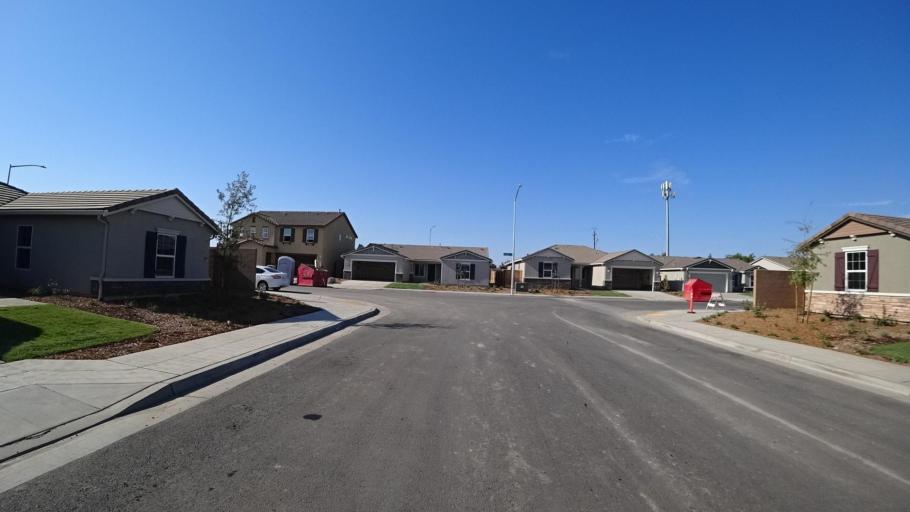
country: US
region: California
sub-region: Fresno County
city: Sunnyside
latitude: 36.7656
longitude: -119.6616
